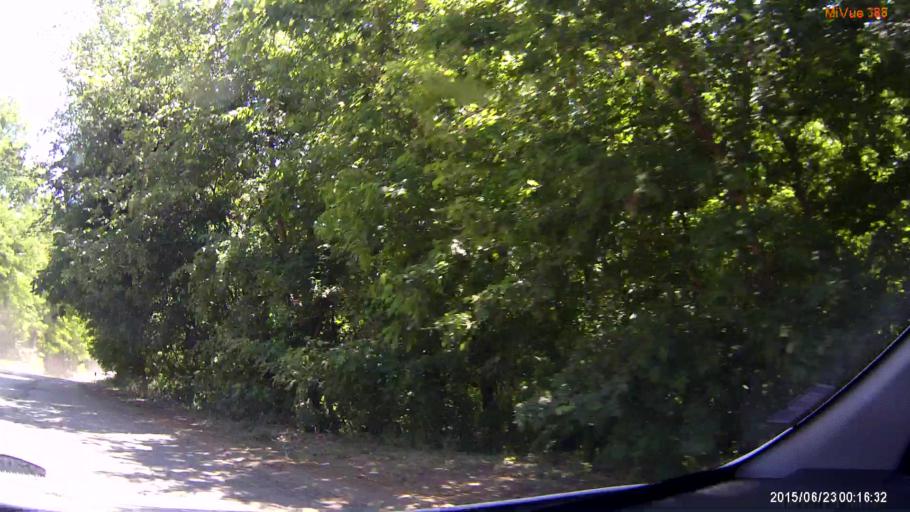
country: RO
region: Iasi
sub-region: Comuna Prisacani
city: Prisacani
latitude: 47.0708
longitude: 27.9522
